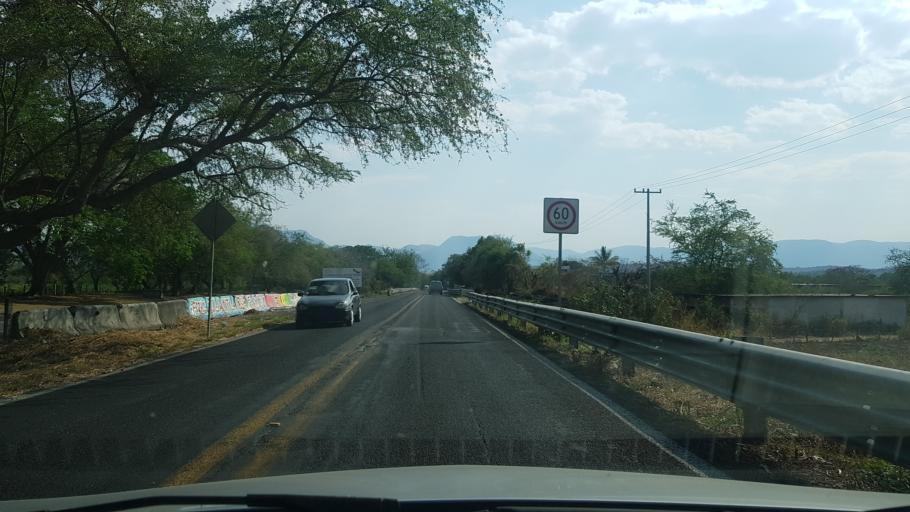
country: MX
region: Morelos
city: Puente de Ixtla
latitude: 18.6243
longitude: -99.3306
